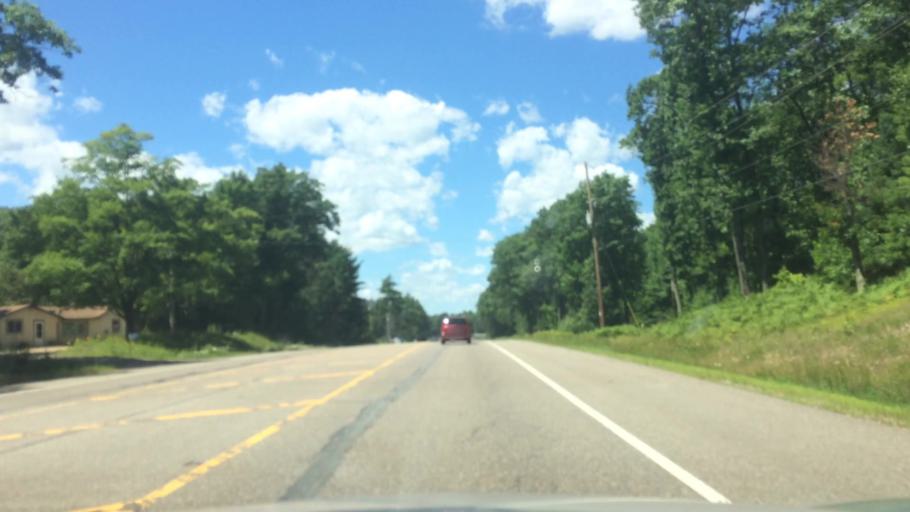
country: US
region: Wisconsin
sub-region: Vilas County
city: Lac du Flambeau
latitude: 45.7938
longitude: -89.7152
